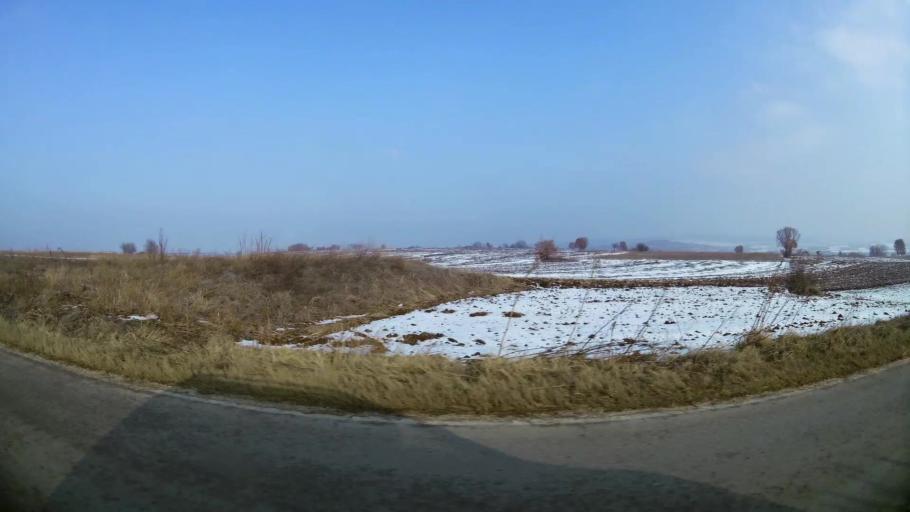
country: MK
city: Miladinovci
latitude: 41.9748
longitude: 21.6318
